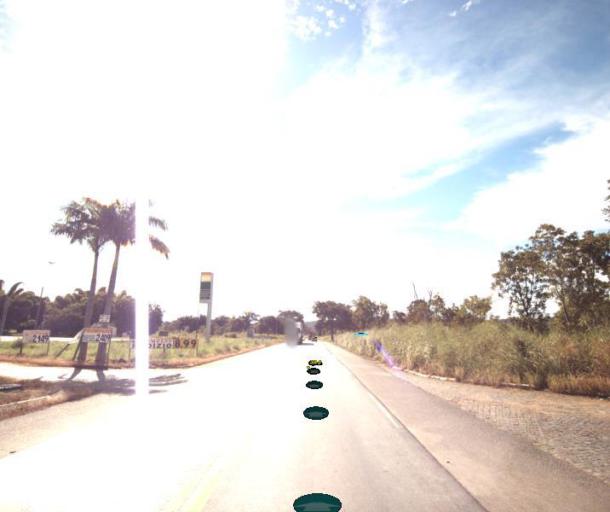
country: BR
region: Goias
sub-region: Jaragua
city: Jaragua
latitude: -15.5612
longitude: -49.4224
